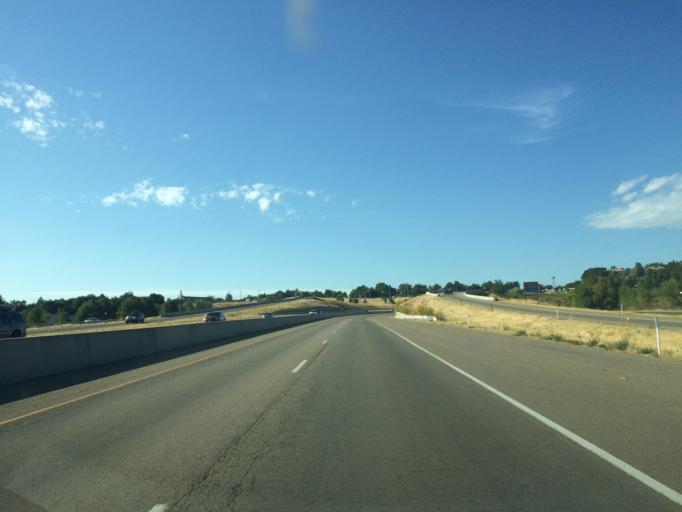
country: US
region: Utah
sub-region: Davis County
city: Fruit Heights
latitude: 41.0068
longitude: -111.9108
